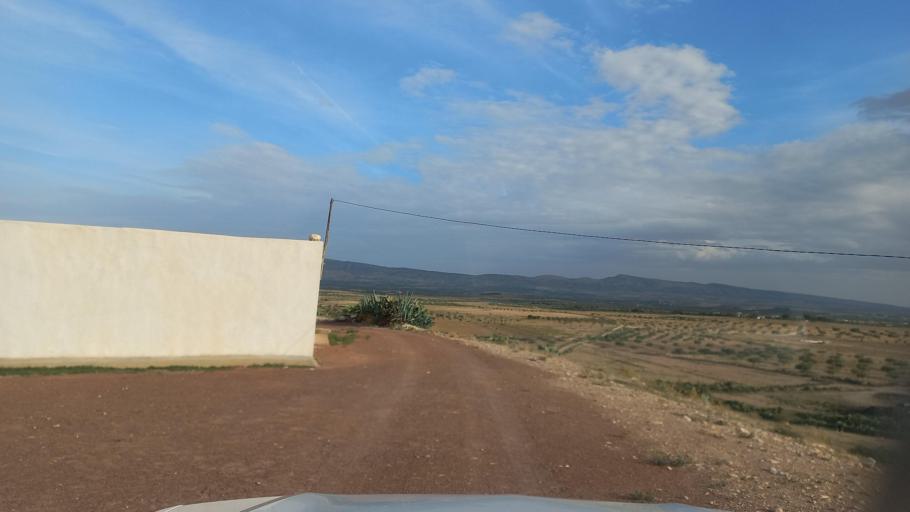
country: TN
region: Al Qasrayn
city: Sbiba
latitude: 35.4530
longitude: 9.0882
